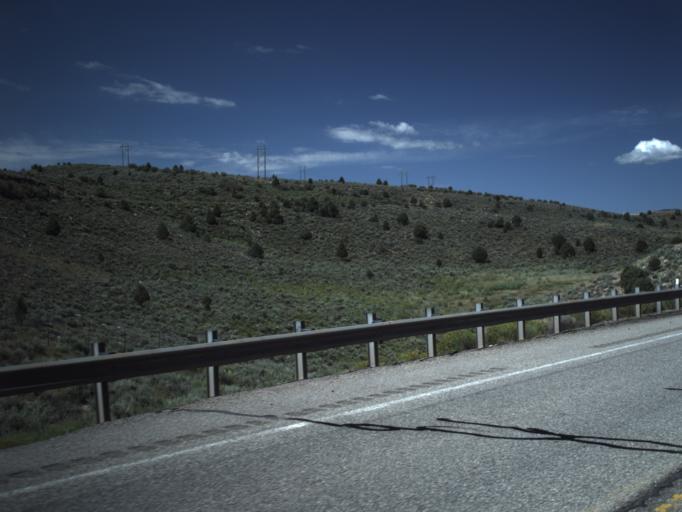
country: US
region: Utah
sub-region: Carbon County
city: Helper
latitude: 39.8259
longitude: -110.9521
